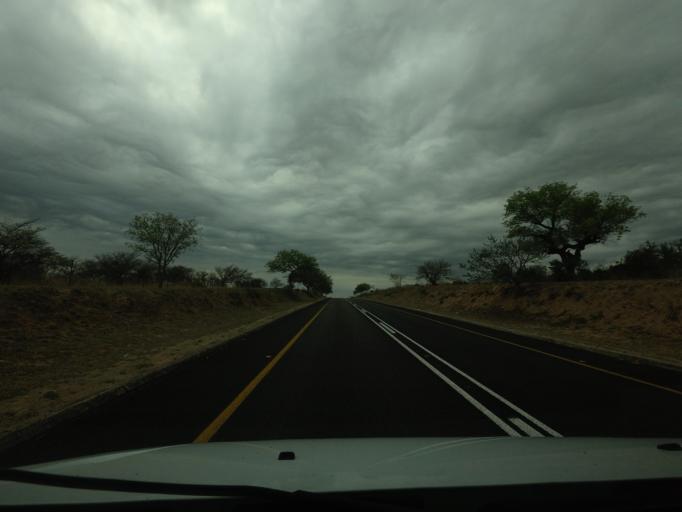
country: ZA
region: Limpopo
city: Thulamahashi
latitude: -24.5682
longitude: 31.0640
